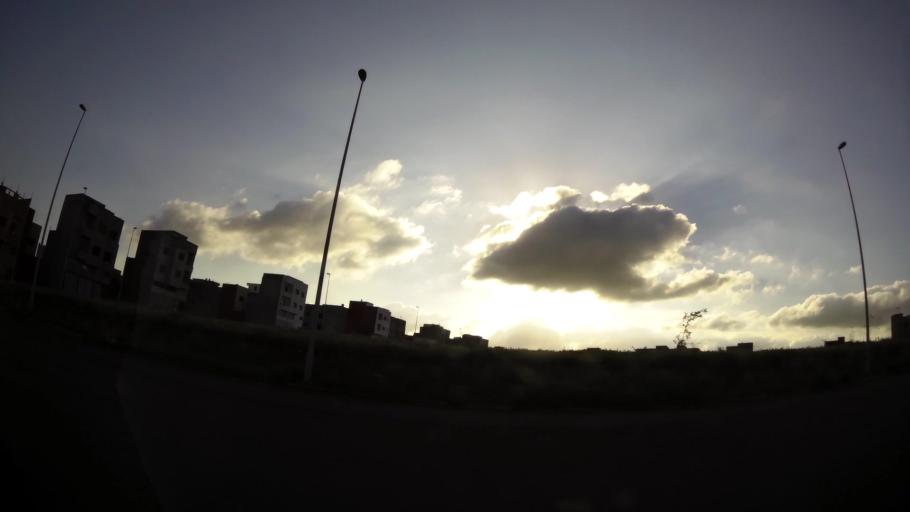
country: MA
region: Chaouia-Ouardigha
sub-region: Settat Province
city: Settat
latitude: 32.9916
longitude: -7.6324
